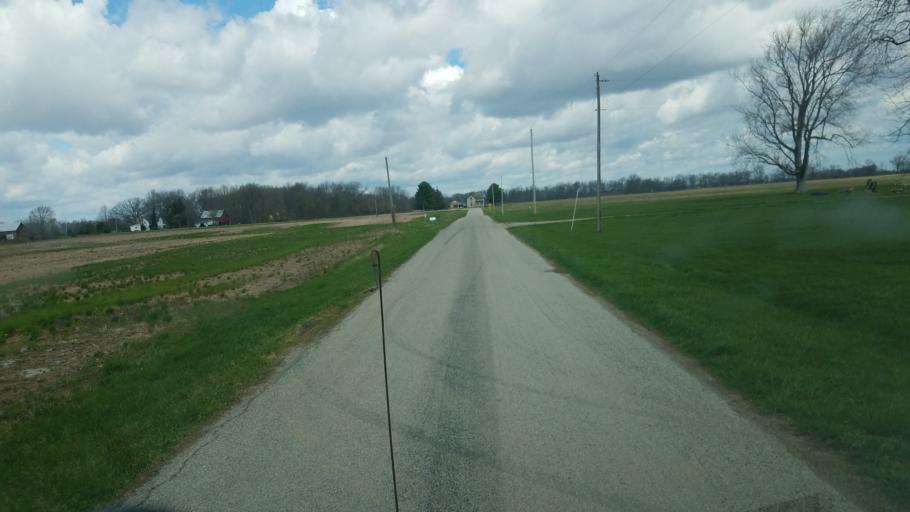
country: US
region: Ohio
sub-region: Union County
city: Richwood
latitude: 40.3831
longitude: -83.2602
